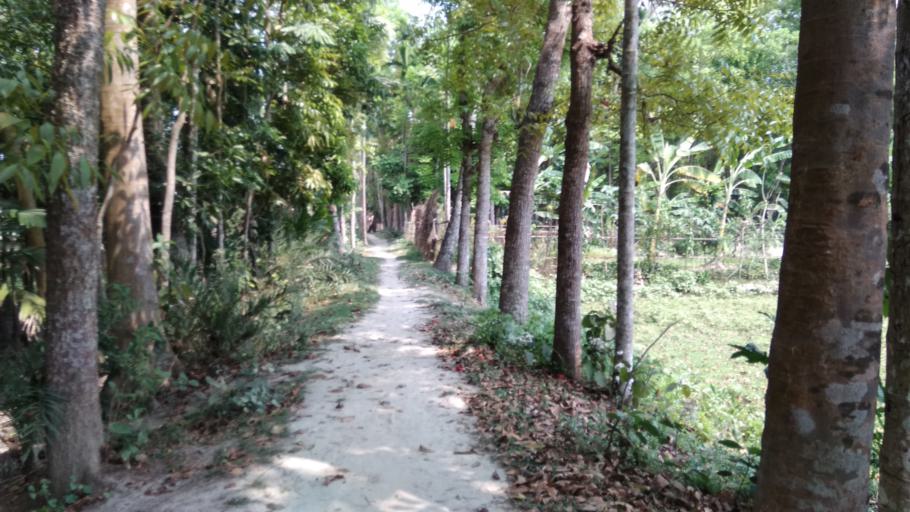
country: BD
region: Barisal
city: Mehendiganj
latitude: 22.9369
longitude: 90.4157
